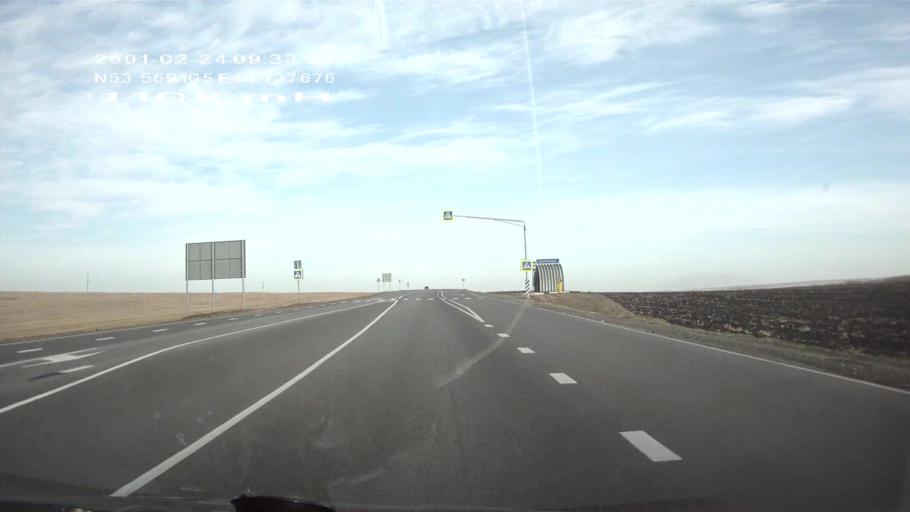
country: RU
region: Penza
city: Mokshan
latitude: 53.5691
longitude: 44.7277
